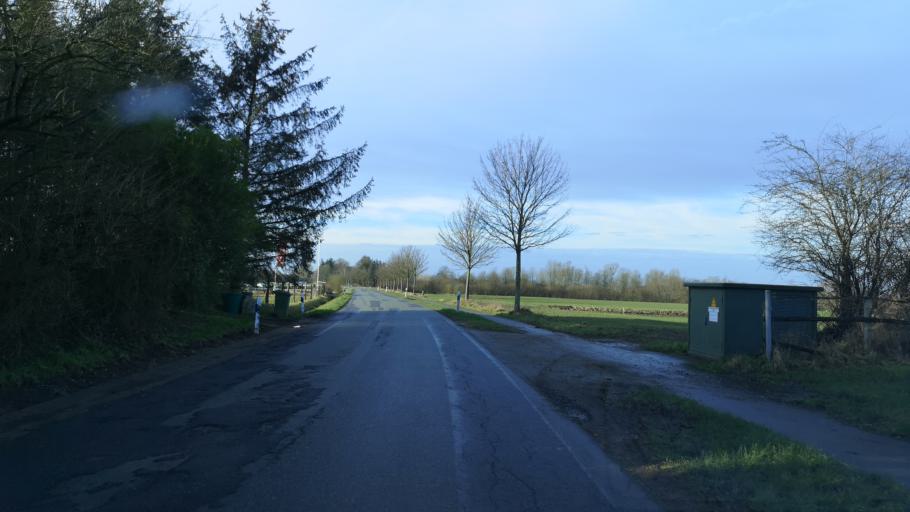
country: DE
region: Schleswig-Holstein
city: Havetoft
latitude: 54.6603
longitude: 9.5418
